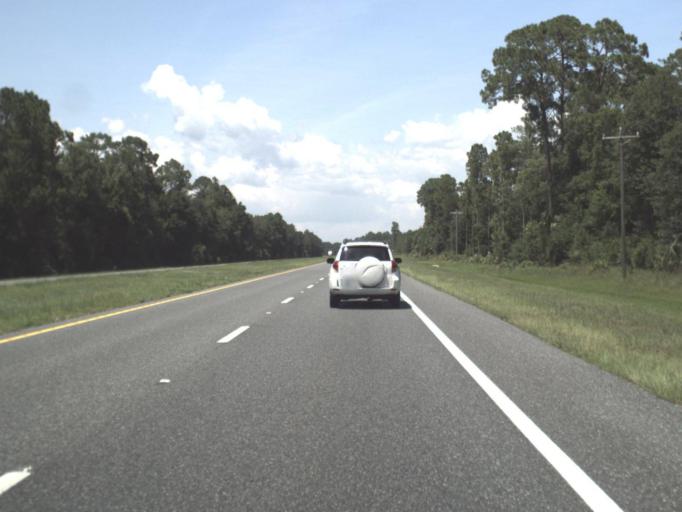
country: US
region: Florida
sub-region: Levy County
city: Inglis
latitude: 29.0807
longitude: -82.6407
